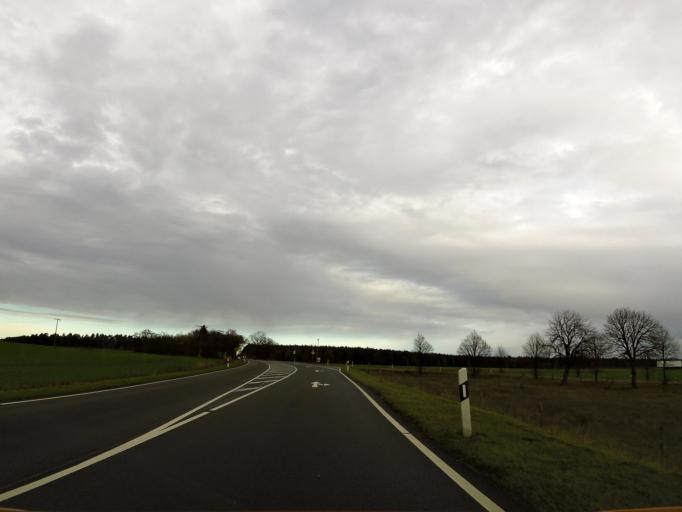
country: DE
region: Saxony-Anhalt
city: Letzlingen
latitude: 52.3766
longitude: 11.4640
